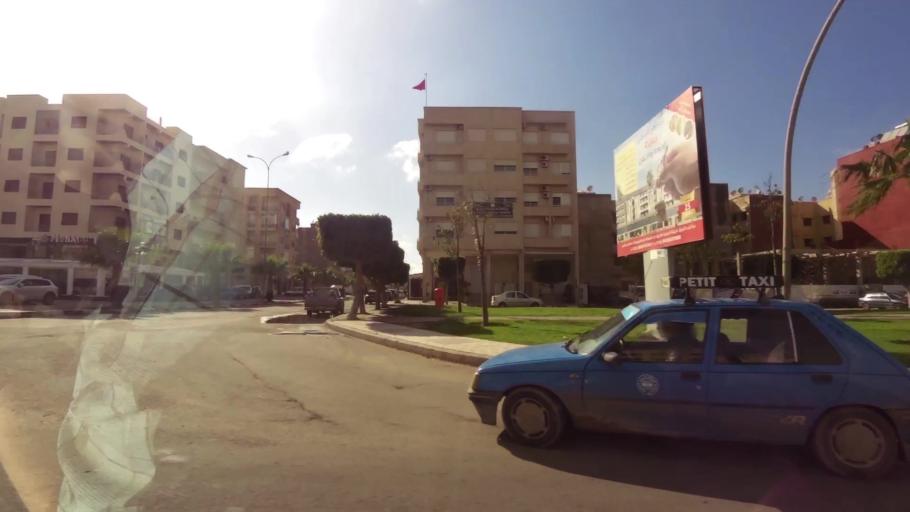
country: MA
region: Chaouia-Ouardigha
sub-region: Settat Province
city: Berrechid
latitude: 33.2744
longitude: -7.5836
